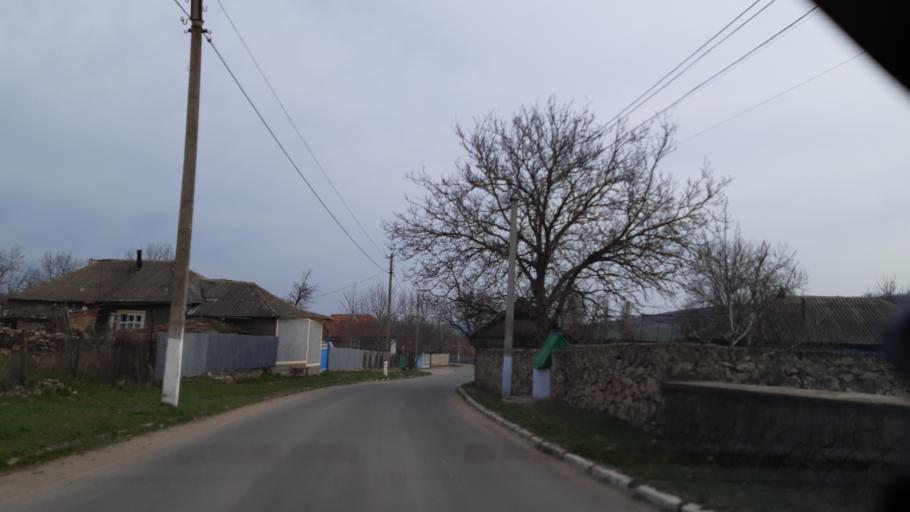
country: MD
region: Soldanesti
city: Soldanesti
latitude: 47.6849
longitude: 28.7790
